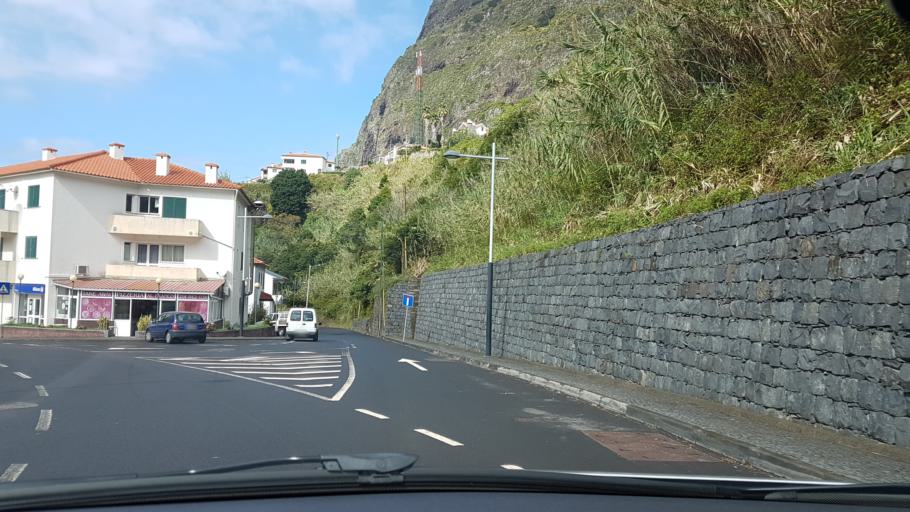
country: PT
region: Madeira
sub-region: Sao Vicente
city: Sao Vicente
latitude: 32.8015
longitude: -17.0424
